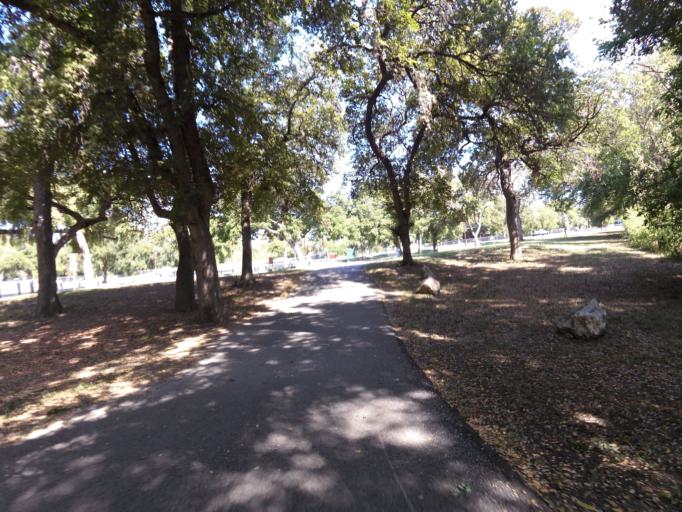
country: US
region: Texas
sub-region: Bexar County
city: China Grove
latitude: 29.3985
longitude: -98.4230
